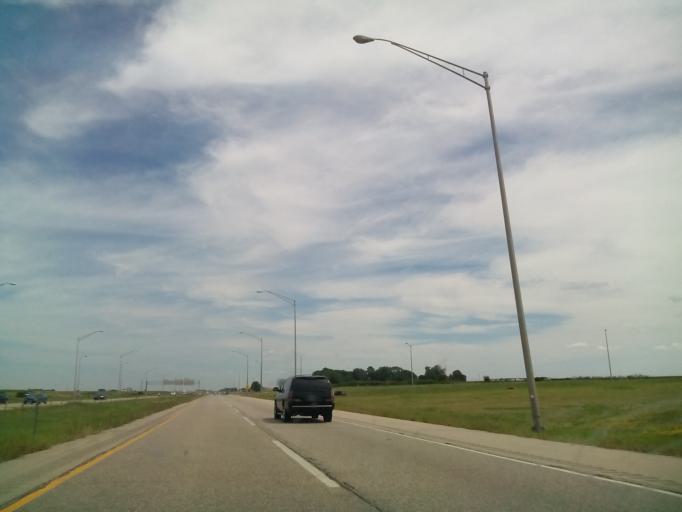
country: US
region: Illinois
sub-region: DeKalb County
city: Cortland
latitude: 41.9003
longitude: -88.7220
